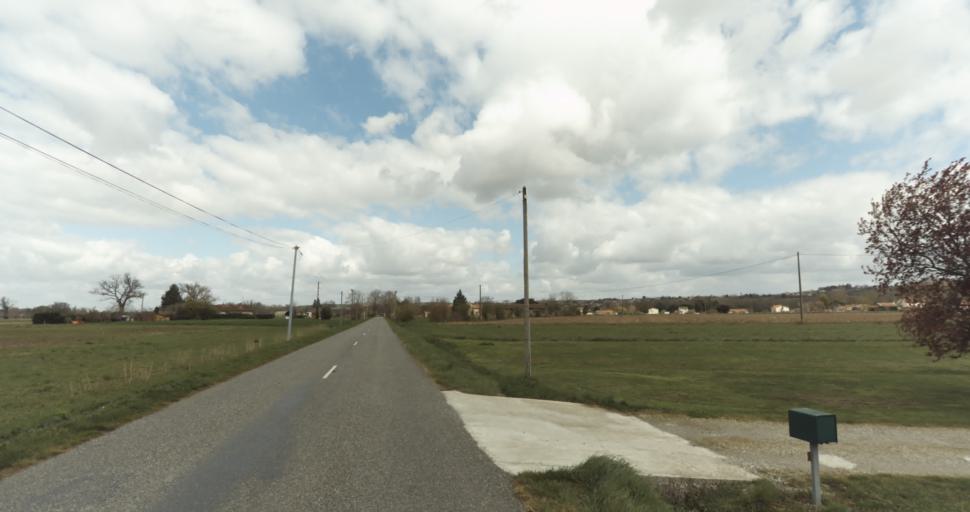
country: FR
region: Midi-Pyrenees
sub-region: Departement de la Haute-Garonne
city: Auterive
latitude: 43.3324
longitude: 1.4786
